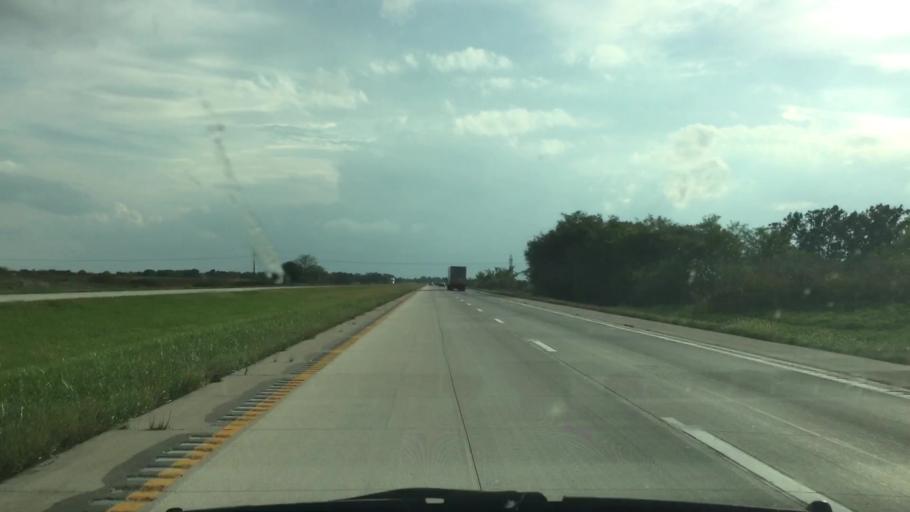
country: US
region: Missouri
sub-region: Daviess County
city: Gallatin
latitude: 39.9663
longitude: -94.0996
